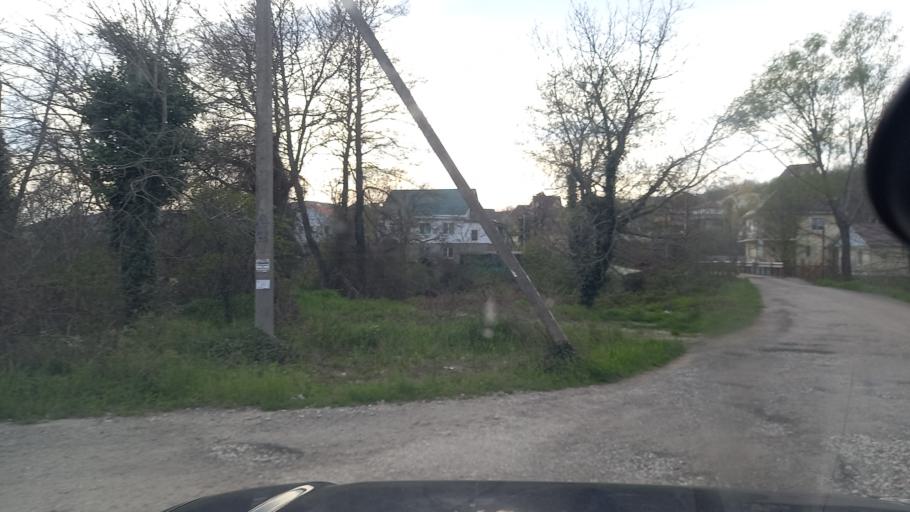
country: RU
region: Krasnodarskiy
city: Arkhipo-Osipovka
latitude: 44.3679
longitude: 38.5452
